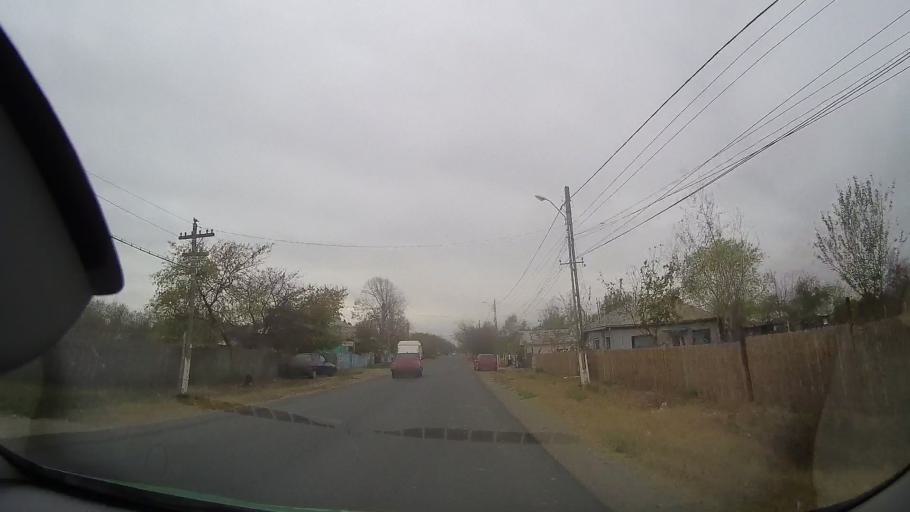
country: RO
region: Braila
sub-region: Comuna Ulmu
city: Ulmu
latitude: 44.9514
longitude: 27.3175
